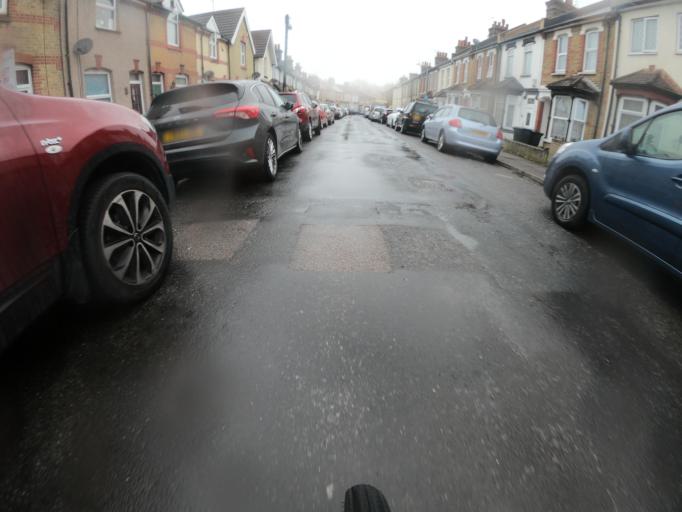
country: GB
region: England
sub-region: Kent
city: Gravesend
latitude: 51.4343
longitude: 0.3515
